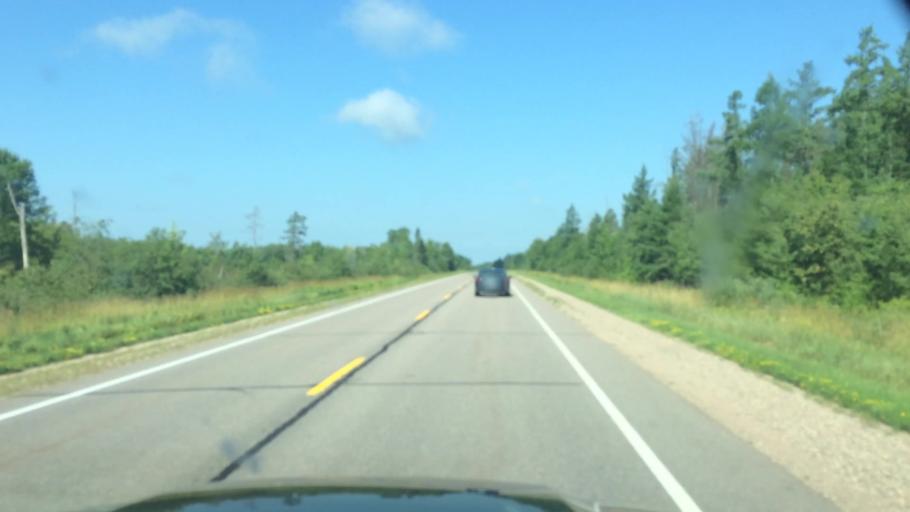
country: US
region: Wisconsin
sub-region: Langlade County
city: Antigo
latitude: 45.1451
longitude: -89.3143
